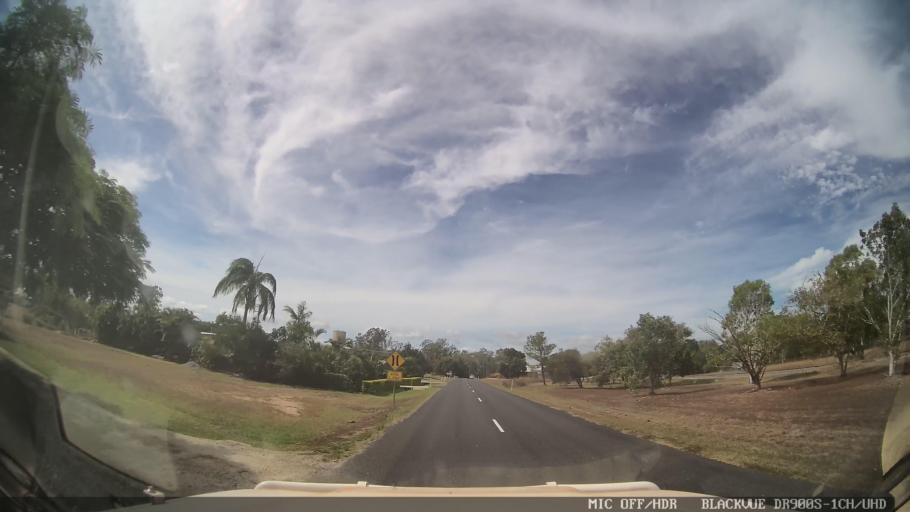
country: AU
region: Queensland
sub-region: Tablelands
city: Mareeba
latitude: -16.9172
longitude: 145.4209
